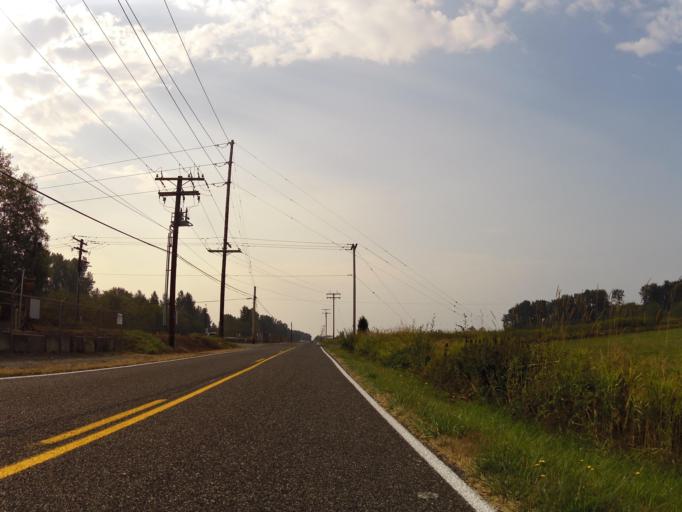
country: US
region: Washington
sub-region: Whatcom County
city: Birch Bay
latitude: 48.8783
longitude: -122.7489
